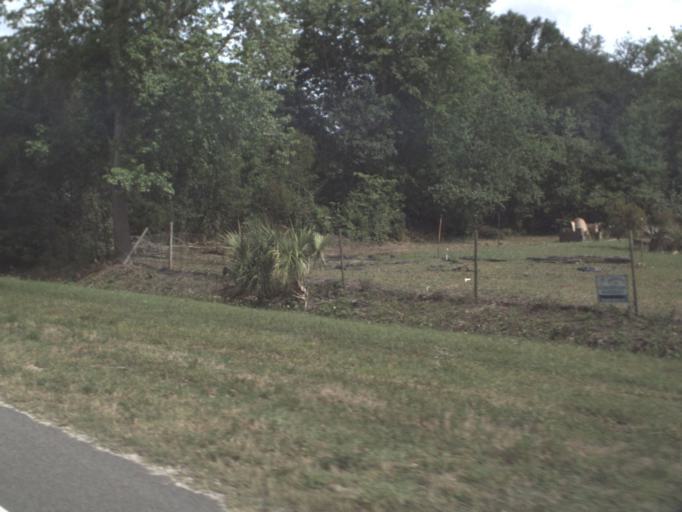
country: US
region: Florida
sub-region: Flagler County
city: Bunnell
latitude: 29.4816
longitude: -81.3836
